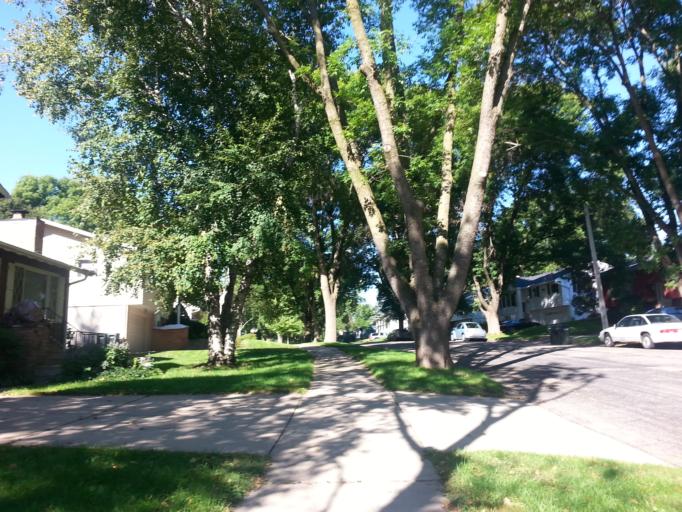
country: US
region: Minnesota
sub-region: Olmsted County
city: Rochester
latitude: 44.0532
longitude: -92.4732
